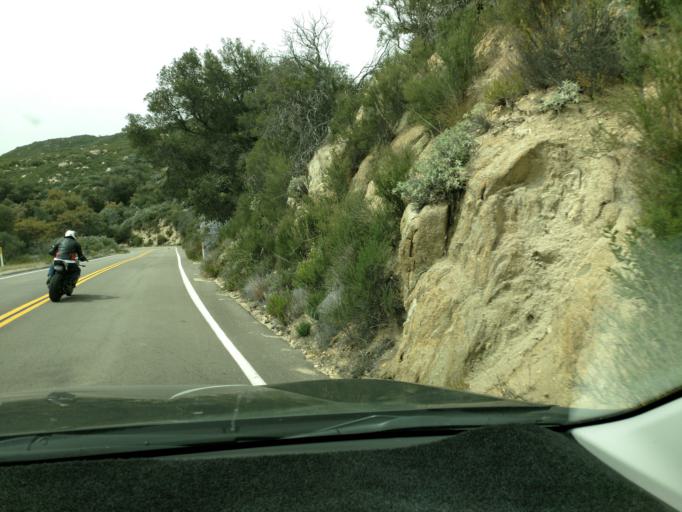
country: US
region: California
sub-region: Riverside County
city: Aguanga
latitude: 33.2527
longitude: -116.7615
